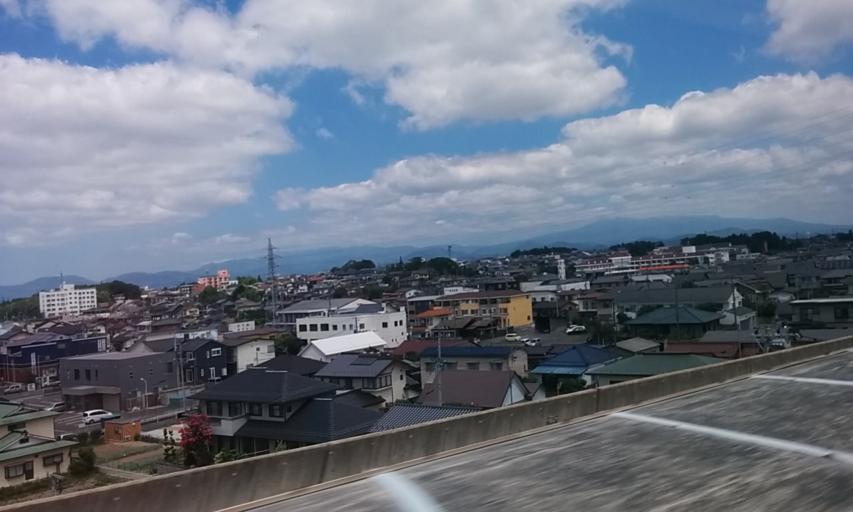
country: JP
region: Fukushima
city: Koriyama
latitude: 37.4130
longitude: 140.3930
